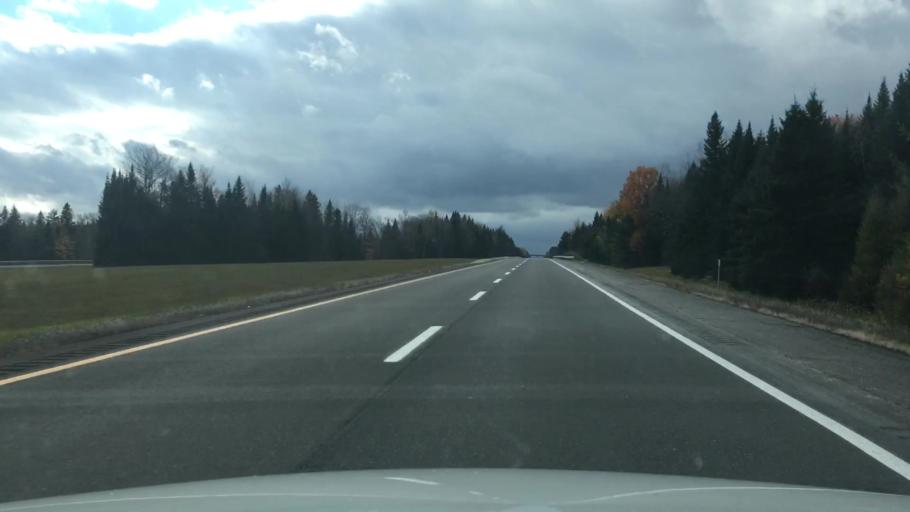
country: US
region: Maine
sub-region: Penobscot County
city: Patten
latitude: 46.1066
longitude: -68.1700
